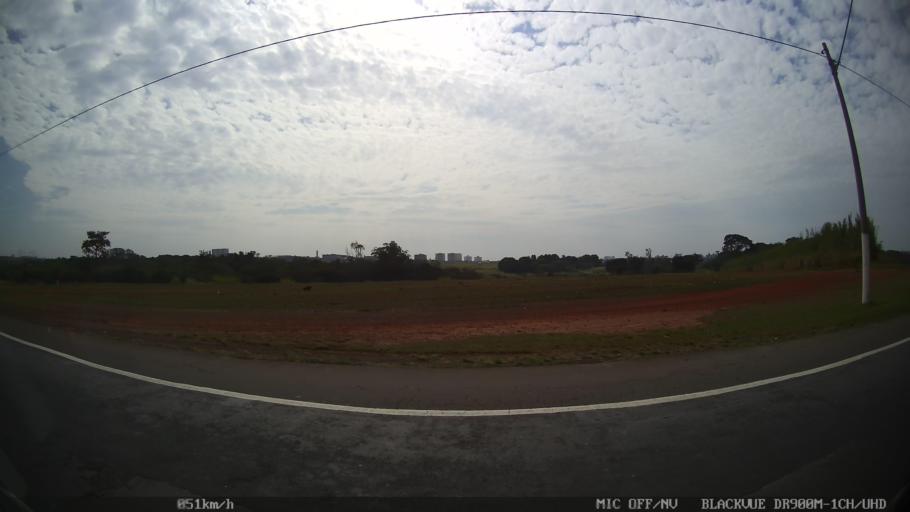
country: BR
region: Sao Paulo
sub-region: Paulinia
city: Paulinia
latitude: -22.7940
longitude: -47.1506
